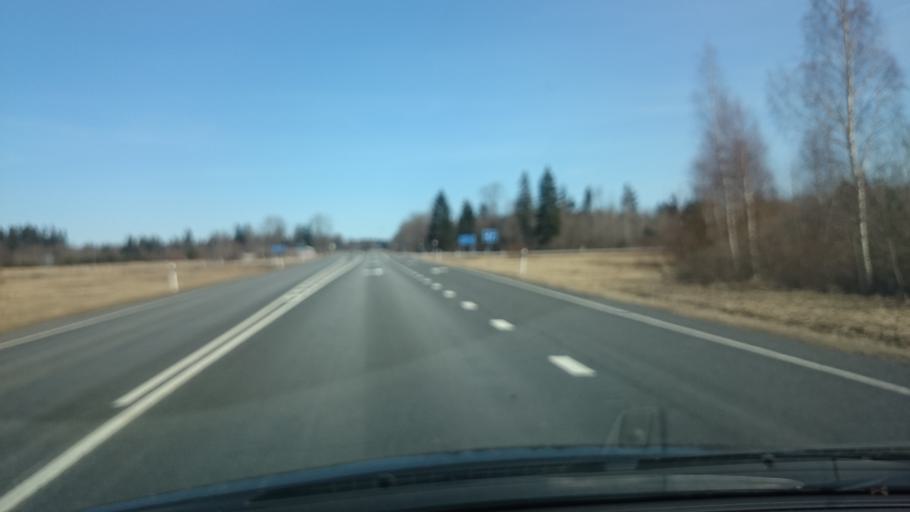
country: EE
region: Paernumaa
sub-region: Vaendra vald (alev)
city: Vandra
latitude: 58.6619
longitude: 25.0217
